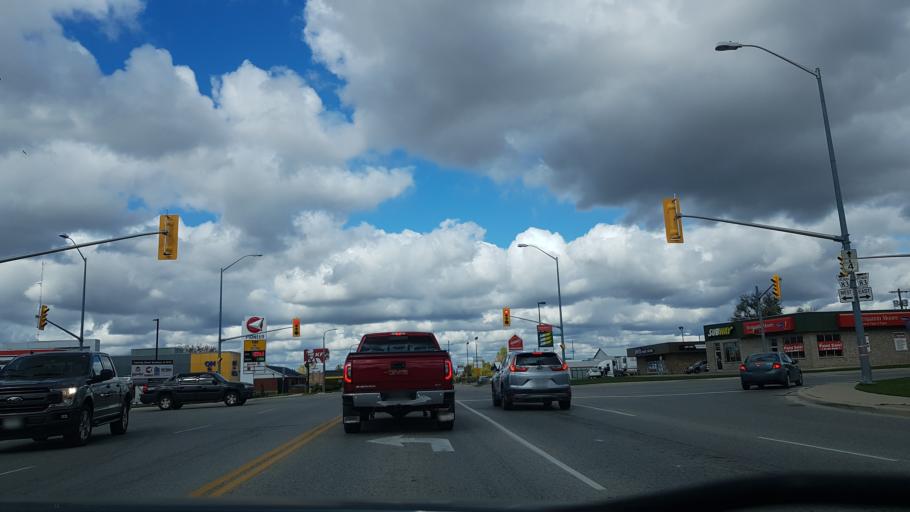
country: CA
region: Ontario
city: South Huron
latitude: 43.3614
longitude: -81.4834
